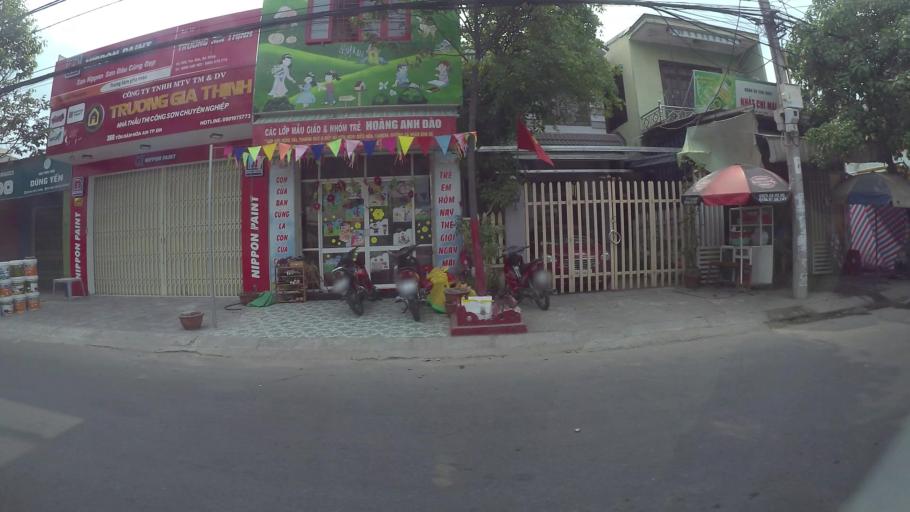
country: VN
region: Da Nang
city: Thanh Khe
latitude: 16.0470
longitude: 108.1818
